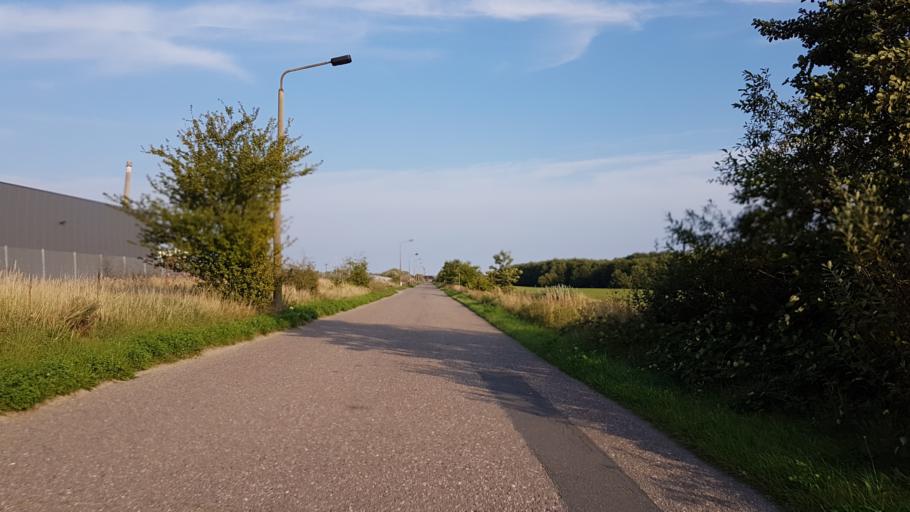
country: DE
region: Mecklenburg-Vorpommern
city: Sagard
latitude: 54.4938
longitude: 13.5588
